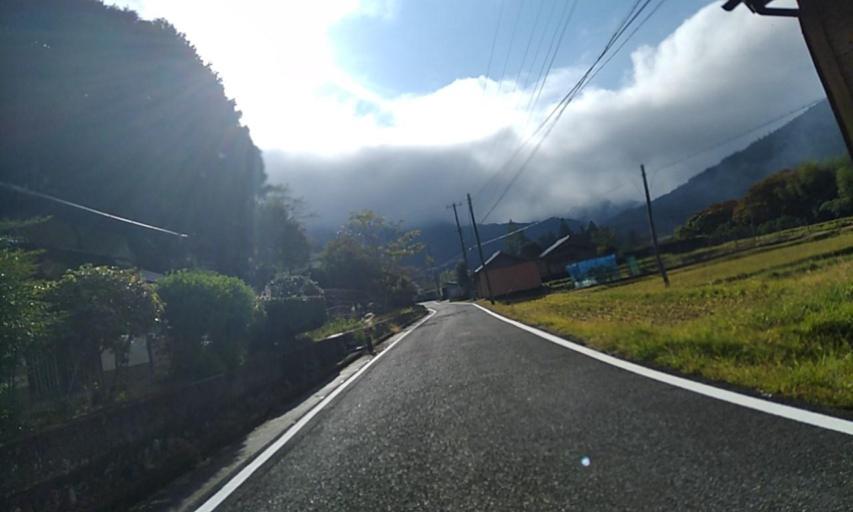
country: JP
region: Wakayama
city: Shingu
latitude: 33.9272
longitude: 135.9811
